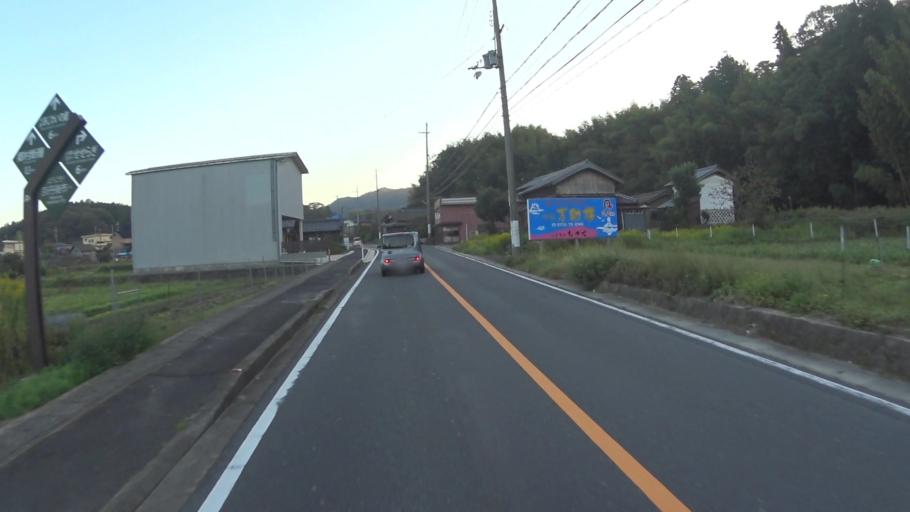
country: JP
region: Kyoto
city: Miyazu
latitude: 35.6543
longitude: 135.0323
